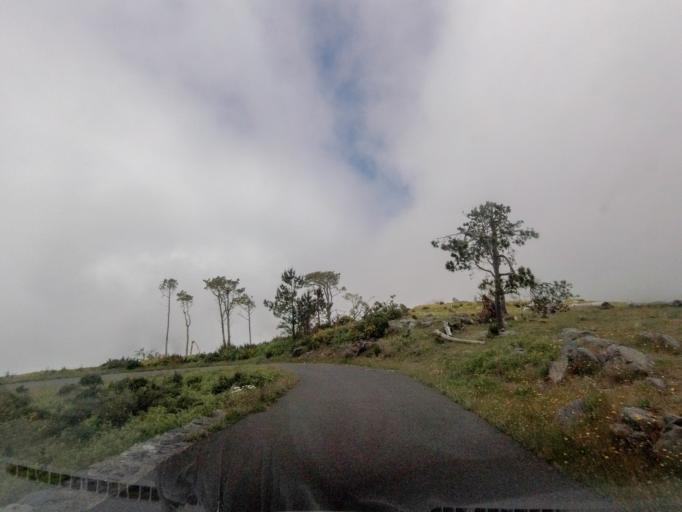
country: PT
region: Madeira
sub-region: Funchal
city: Nossa Senhora do Monte
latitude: 32.7150
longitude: -16.9104
